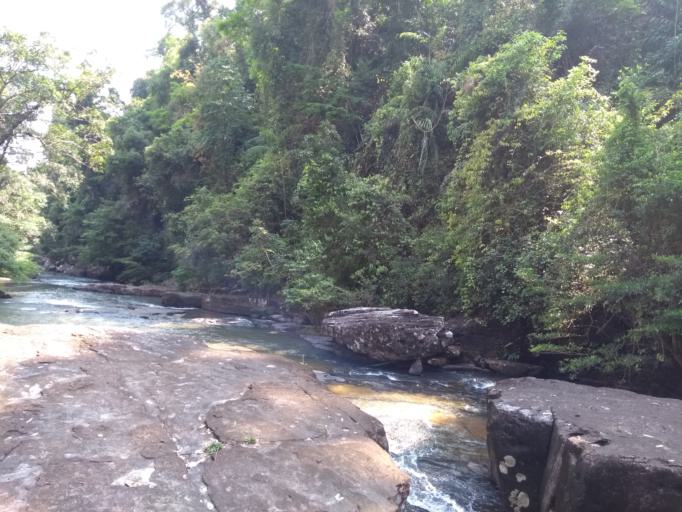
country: TH
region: Trat
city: Ko Kut
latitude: 11.6461
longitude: 102.5564
